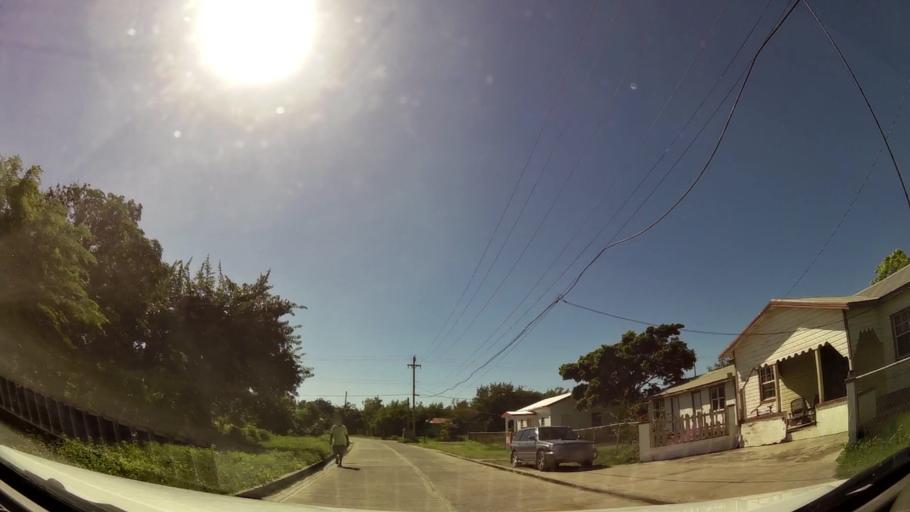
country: AG
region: Barbuda
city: Codrington
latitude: 17.6395
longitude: -61.8278
